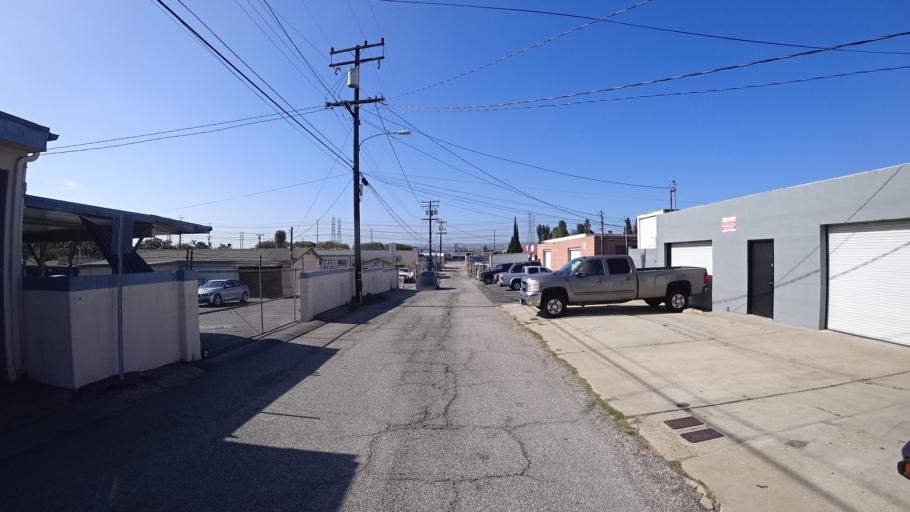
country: US
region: California
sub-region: Los Angeles County
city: Redondo Beach
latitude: 33.8597
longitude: -118.3672
